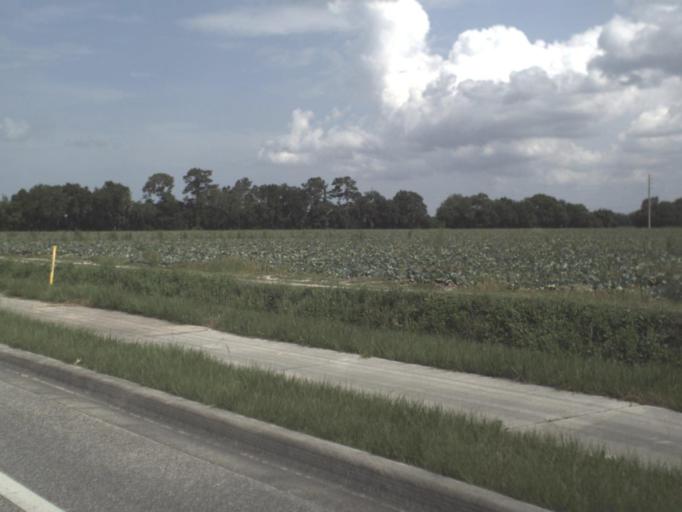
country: US
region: Florida
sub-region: Putnam County
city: East Palatka
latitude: 29.7143
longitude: -81.5028
